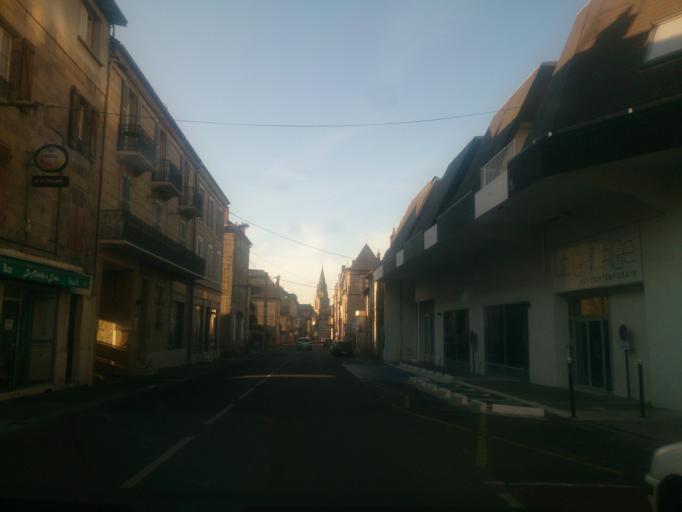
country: FR
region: Limousin
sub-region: Departement de la Correze
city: Brive-la-Gaillarde
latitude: 45.1547
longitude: 1.5330
